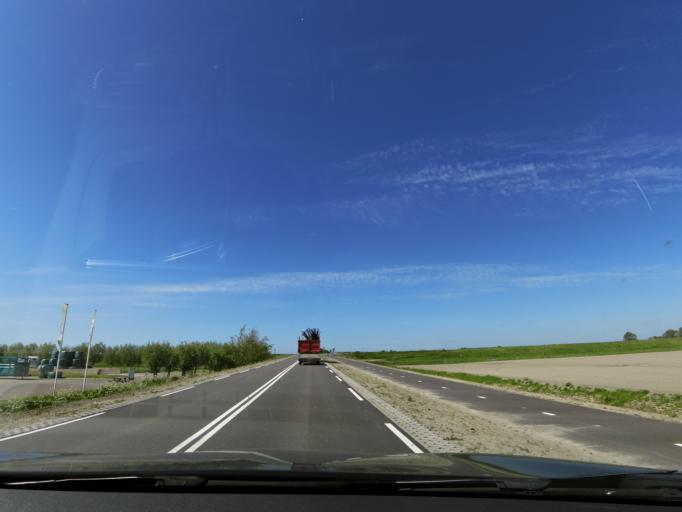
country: NL
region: Zeeland
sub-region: Schouwen-Duiveland
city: Bruinisse
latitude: 51.6728
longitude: 3.9878
